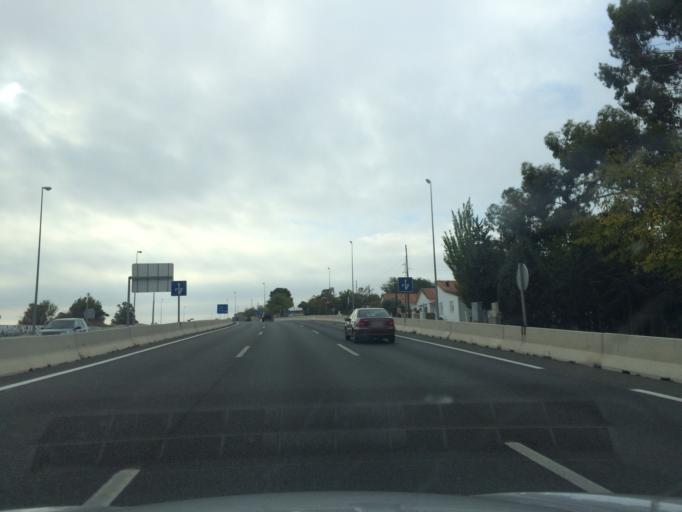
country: ES
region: Madrid
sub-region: Provincia de Madrid
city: Tres Cantos
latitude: 40.5546
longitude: -3.7093
